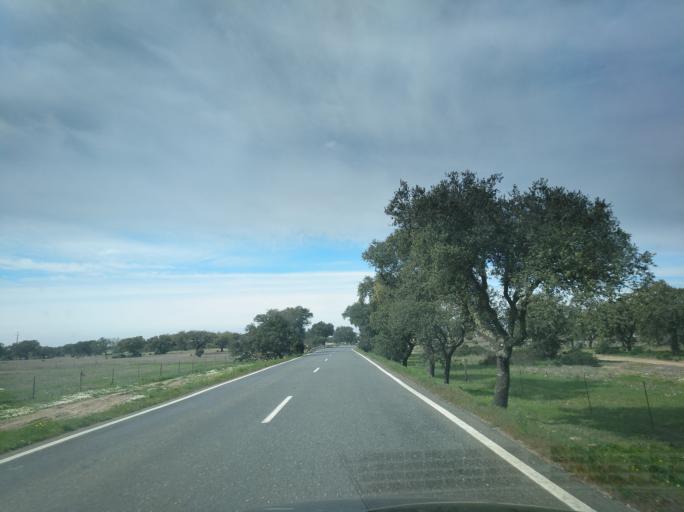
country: PT
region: Beja
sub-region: Mertola
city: Mertola
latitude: 37.7522
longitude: -7.8055
